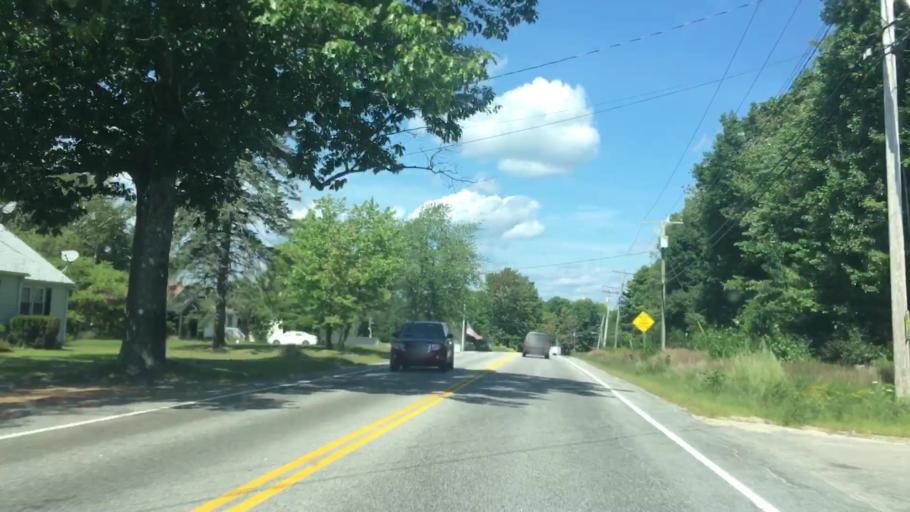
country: US
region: Maine
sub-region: Cumberland County
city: New Gloucester
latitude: 43.8975
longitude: -70.3275
